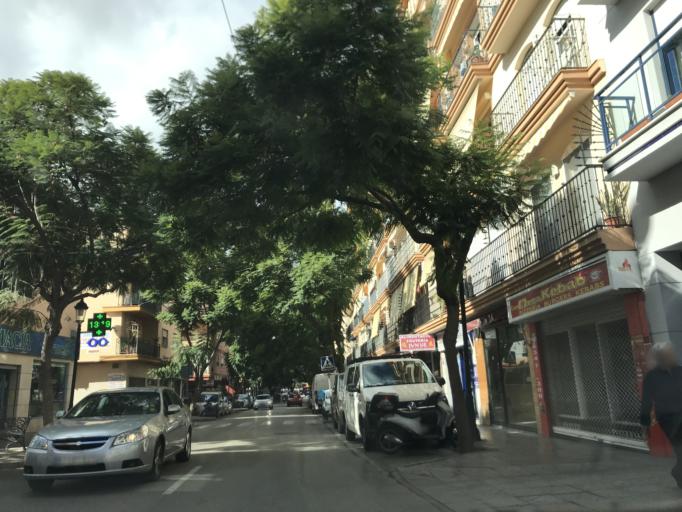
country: ES
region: Andalusia
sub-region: Provincia de Malaga
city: Fuengirola
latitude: 36.5393
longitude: -4.6282
